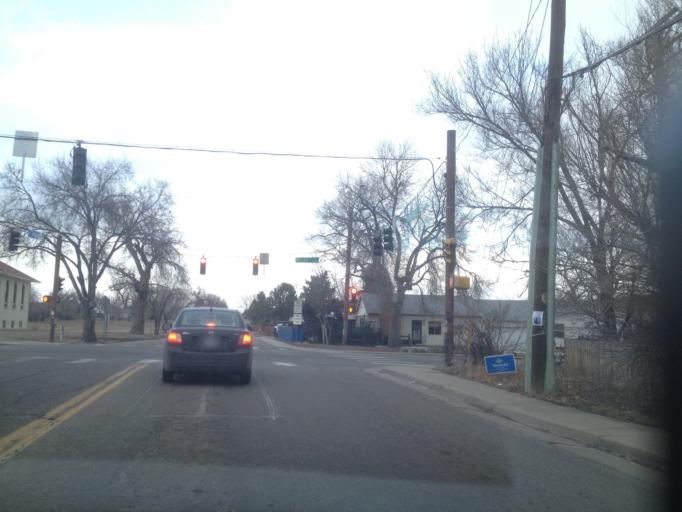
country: US
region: Colorado
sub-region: Adams County
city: Berkley
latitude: 39.8126
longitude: -105.0441
